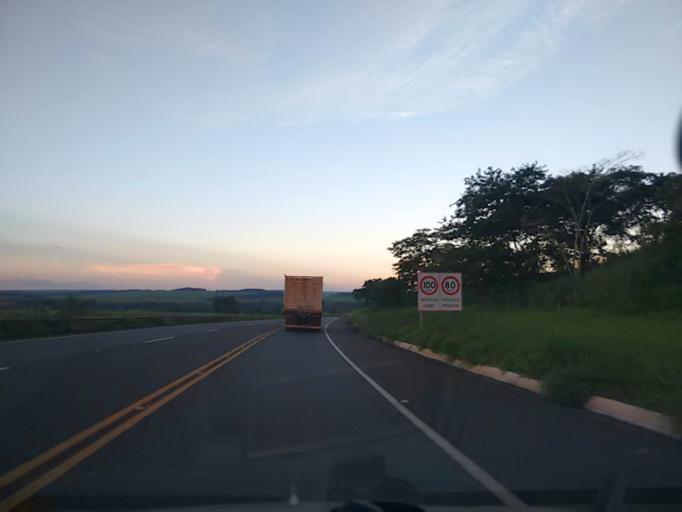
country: BR
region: Sao Paulo
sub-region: Boa Esperanca Do Sul
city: Boa Esperanca do Sul
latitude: -22.0935
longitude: -48.4511
